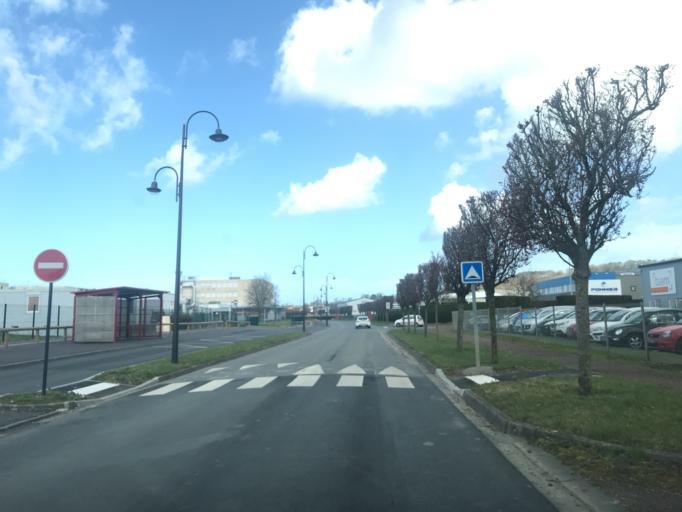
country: FR
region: Lower Normandy
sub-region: Departement du Calvados
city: Dives-sur-Mer
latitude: 49.2777
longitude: -0.0953
